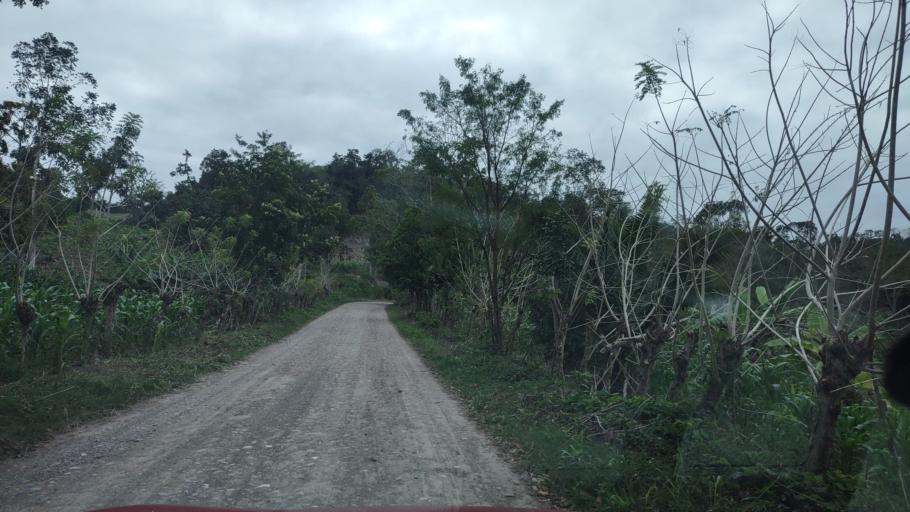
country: MX
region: Veracruz
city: Papantla de Olarte
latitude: 20.4208
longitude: -97.2722
